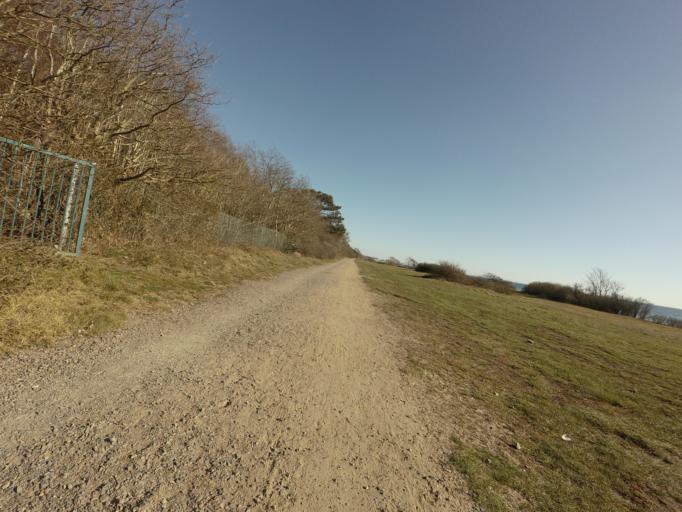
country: SE
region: Skane
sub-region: Helsingborg
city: Helsingborg
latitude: 56.0886
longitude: 12.6495
